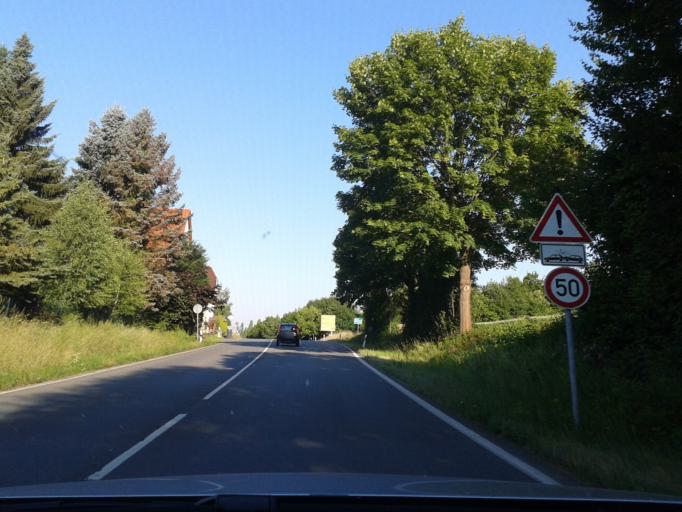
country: DE
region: North Rhine-Westphalia
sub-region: Regierungsbezirk Detmold
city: Dorentrup
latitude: 52.0294
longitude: 9.0326
